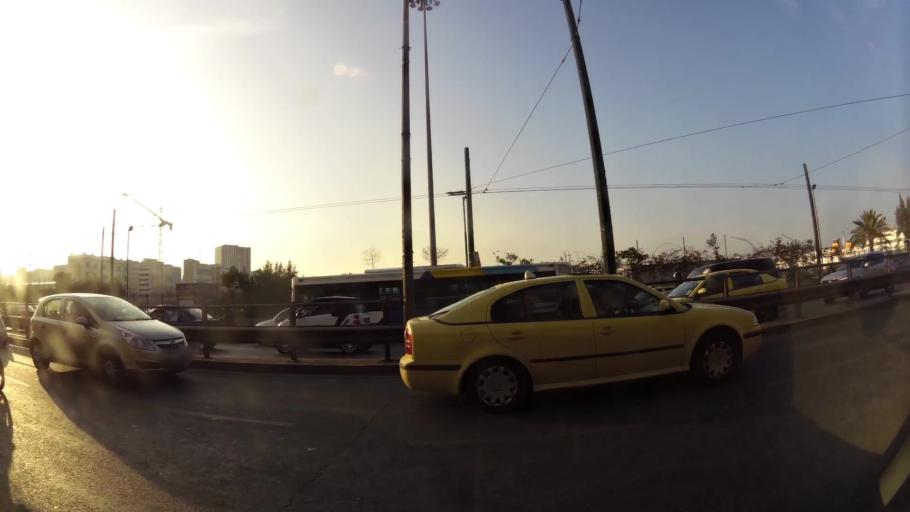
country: GR
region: Attica
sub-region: Nomos Attikis
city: Piraeus
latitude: 37.9494
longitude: 23.6404
